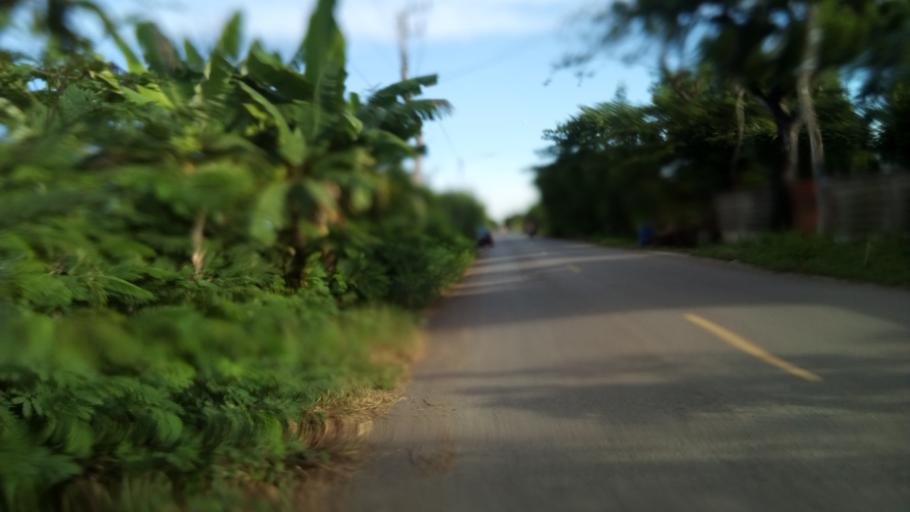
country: TH
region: Pathum Thani
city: Ban Rangsit
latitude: 14.0382
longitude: 100.8476
